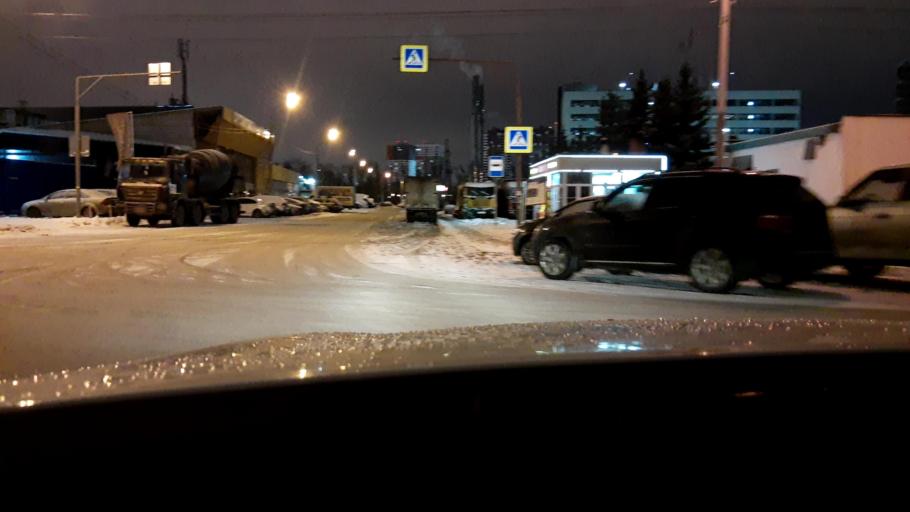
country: RU
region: Moscow
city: Khimki
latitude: 55.9147
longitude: 37.4153
